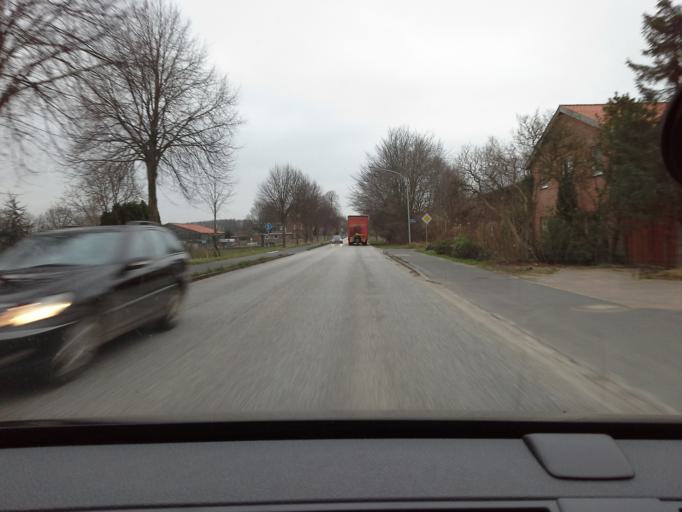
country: DE
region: Schleswig-Holstein
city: Lentfohrden
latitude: 53.8768
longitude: 9.8880
